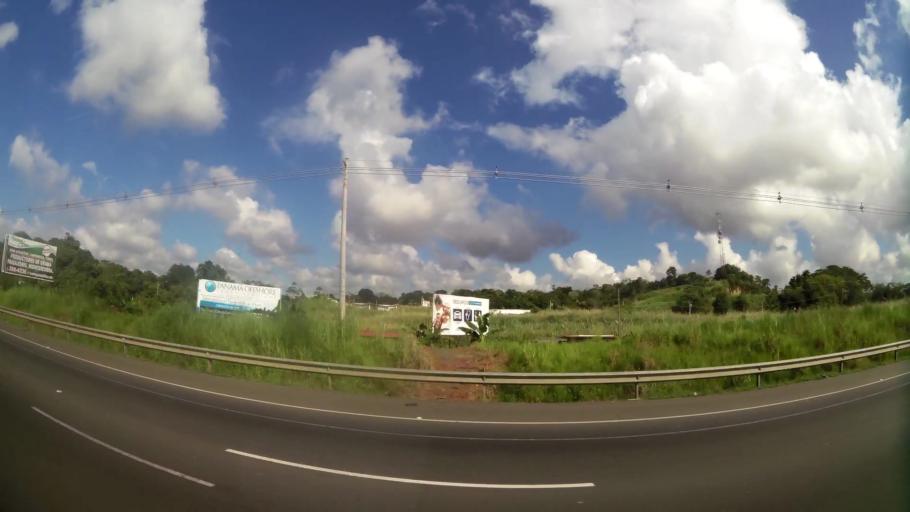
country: PA
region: Panama
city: Nuevo Arraijan
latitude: 8.9156
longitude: -79.7137
